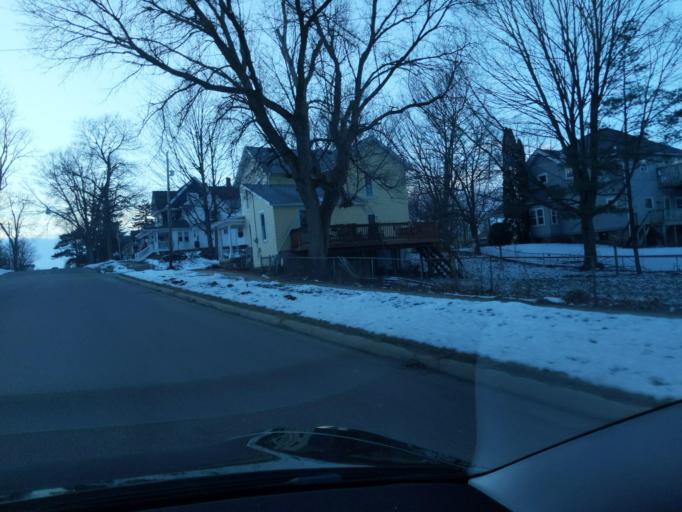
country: US
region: Michigan
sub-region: Ingham County
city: Mason
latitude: 42.5803
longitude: -84.4391
